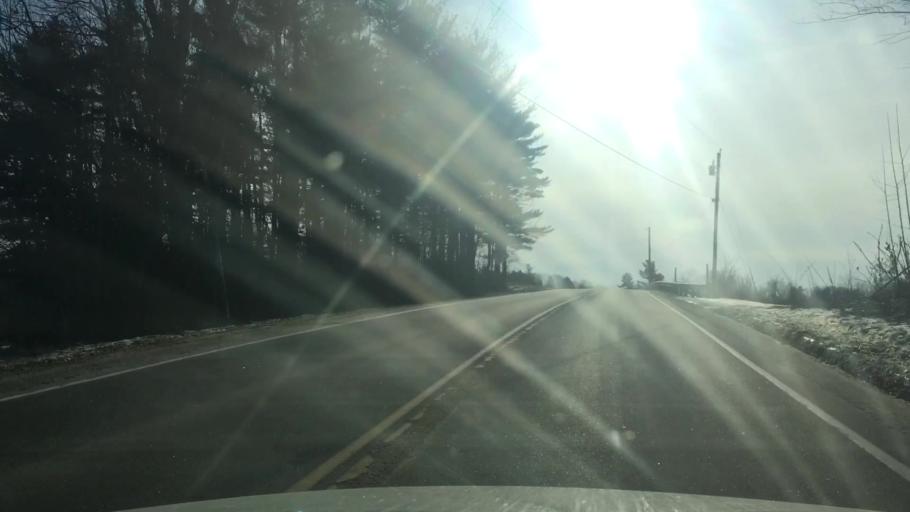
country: US
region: Maine
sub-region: Androscoggin County
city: Sabattus
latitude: 44.1191
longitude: -70.0866
